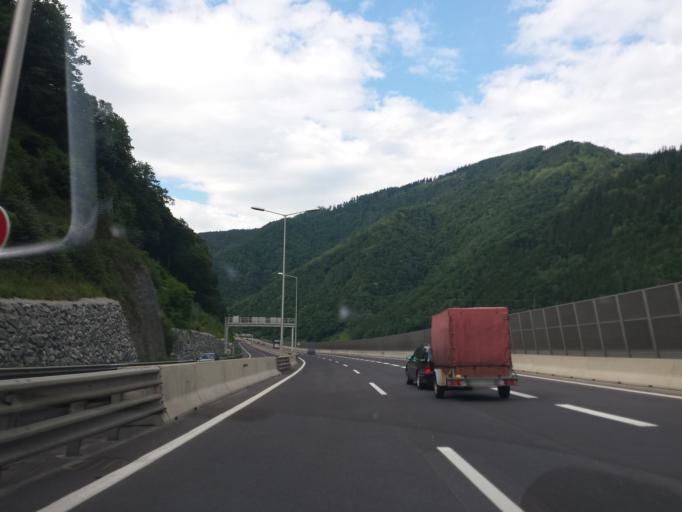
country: AT
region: Styria
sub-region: Politischer Bezirk Bruck-Muerzzuschlag
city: Pernegg an der Mur
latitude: 47.3810
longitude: 15.3063
